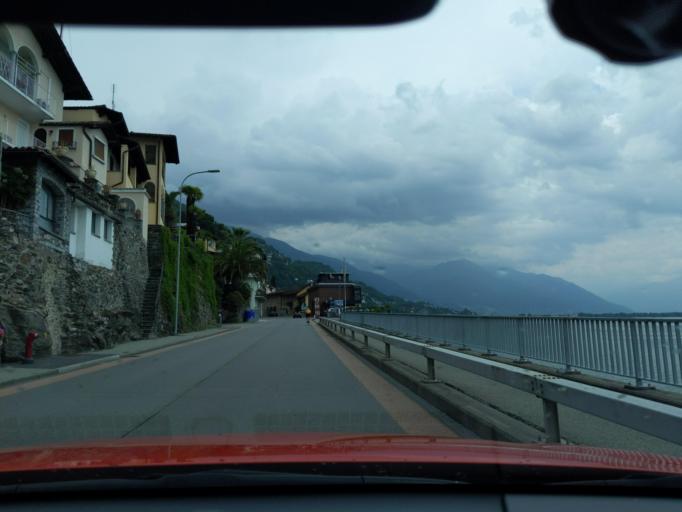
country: CH
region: Ticino
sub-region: Locarno District
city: Brissago
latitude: 46.1392
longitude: 8.7249
